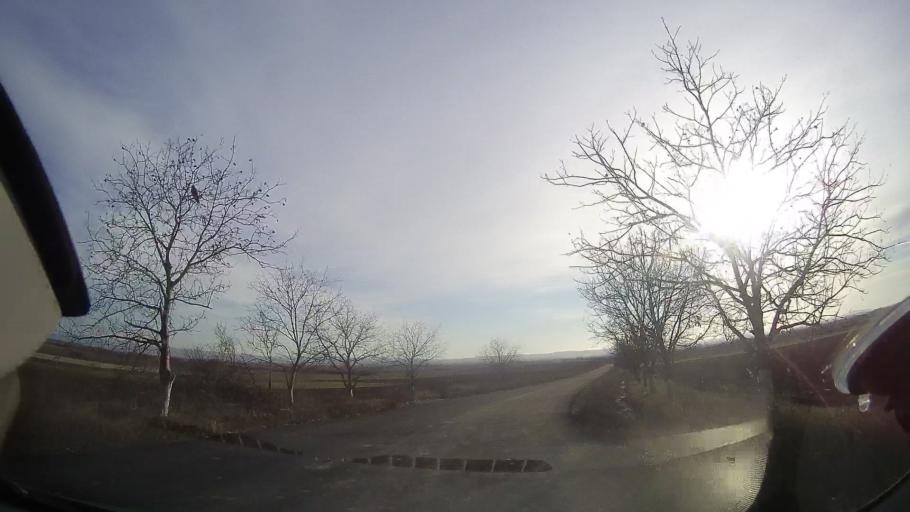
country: RO
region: Bihor
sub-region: Comuna Tileagd
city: Tileagd
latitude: 47.0929
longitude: 22.1783
